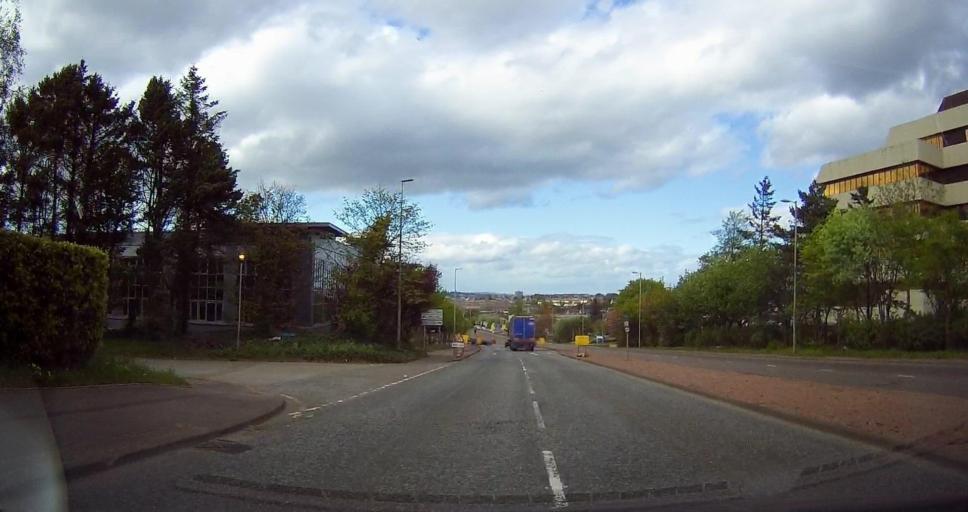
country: GB
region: Scotland
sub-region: Aberdeen City
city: Aberdeen
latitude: 57.1206
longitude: -2.0887
